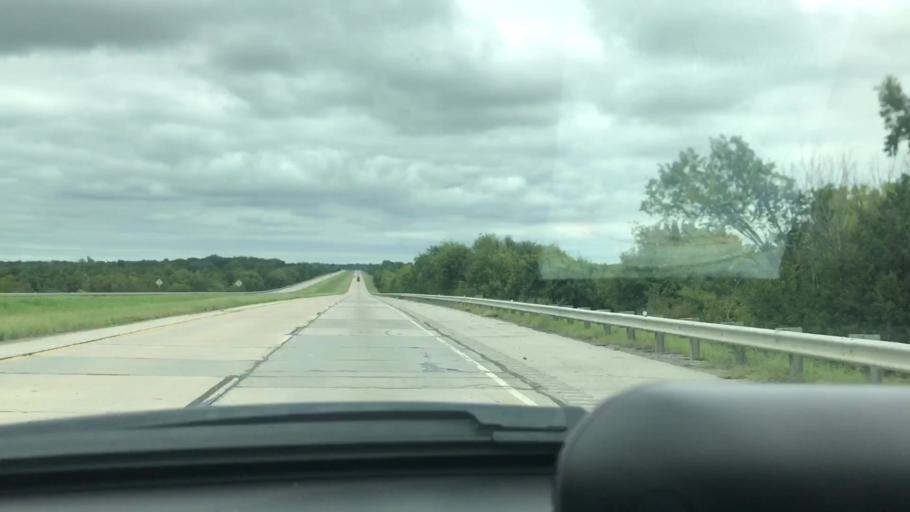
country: US
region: Oklahoma
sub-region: Wagoner County
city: Wagoner
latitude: 35.8876
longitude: -95.4025
